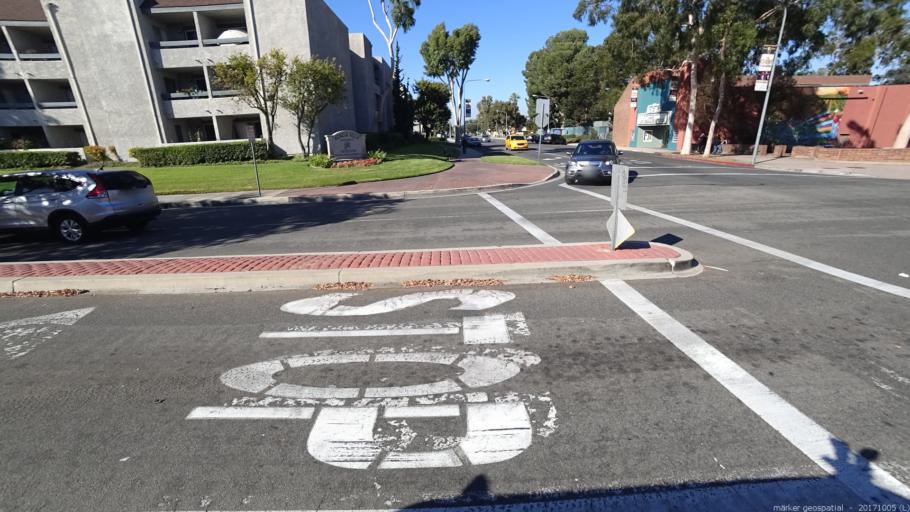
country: US
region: California
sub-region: Orange County
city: Garden Grove
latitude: 33.7759
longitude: -117.9412
